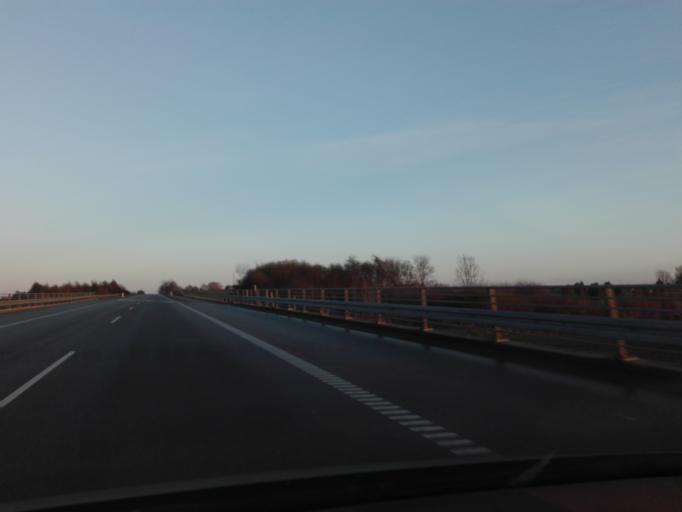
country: DK
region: Central Jutland
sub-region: Skanderborg Kommune
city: Skovby
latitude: 56.1507
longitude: 9.9777
